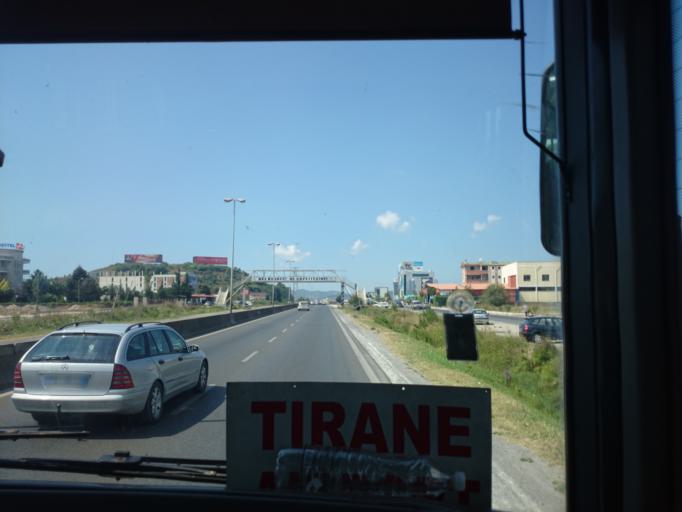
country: AL
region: Tirane
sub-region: Rrethi i Tiranes
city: Kashar
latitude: 41.3579
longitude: 19.7331
